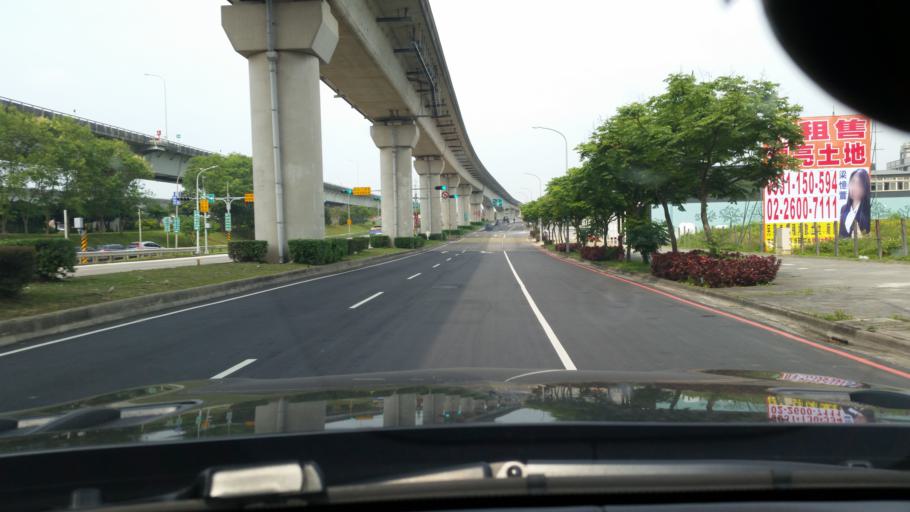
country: TW
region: Taiwan
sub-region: Taoyuan
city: Taoyuan
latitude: 25.0659
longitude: 121.3582
